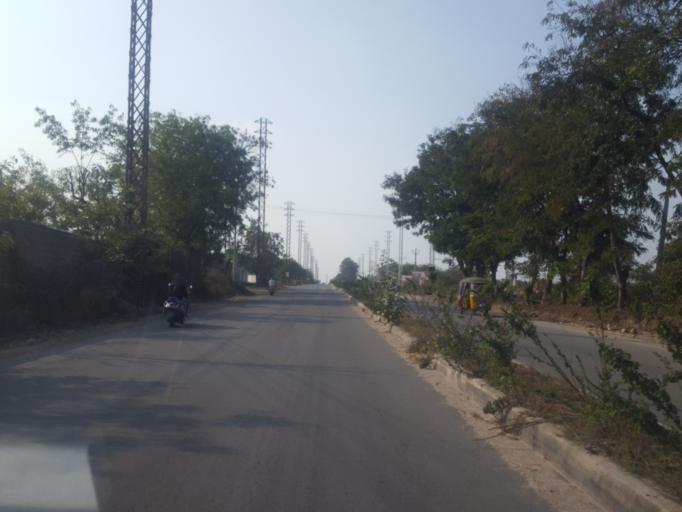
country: IN
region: Telangana
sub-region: Medak
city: Serilingampalle
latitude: 17.4140
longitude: 78.2638
